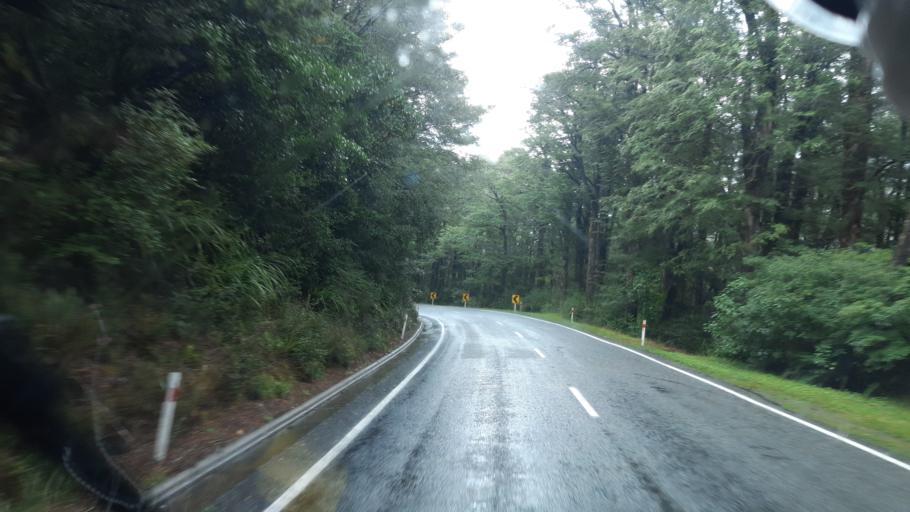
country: NZ
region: Canterbury
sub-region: Hurunui District
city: Amberley
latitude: -42.3778
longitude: 172.3475
